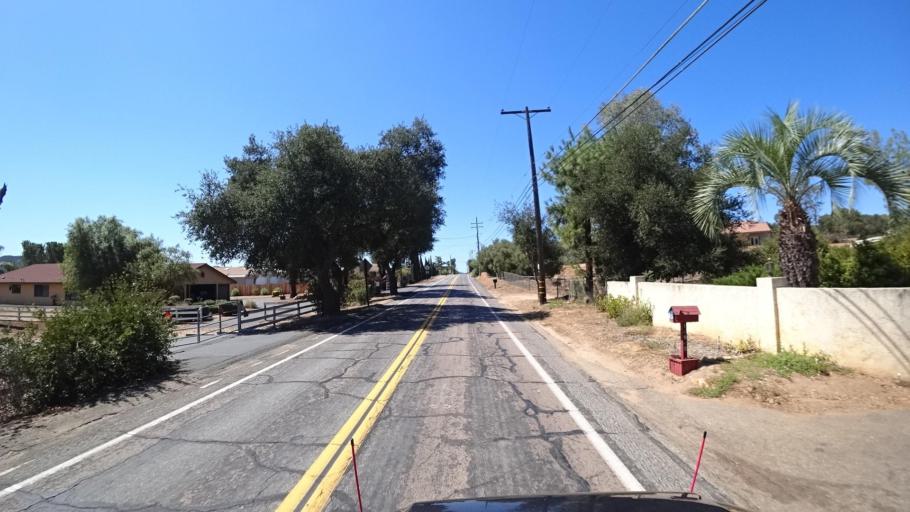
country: US
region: California
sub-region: San Diego County
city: Valley Center
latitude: 33.2348
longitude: -117.0083
